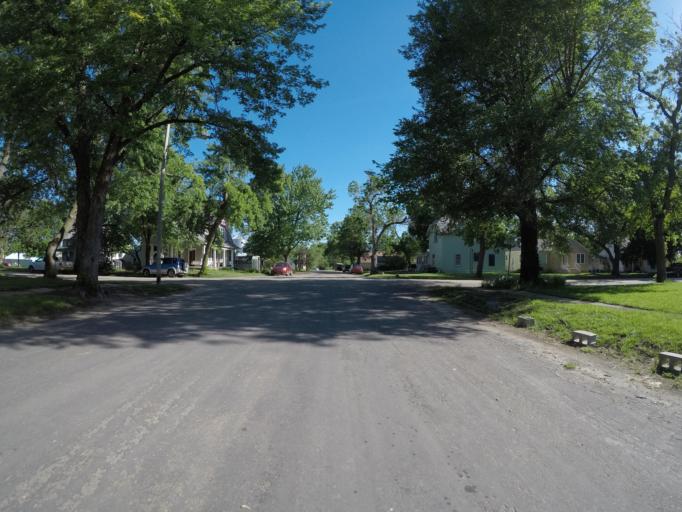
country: US
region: Kansas
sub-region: Riley County
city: Fort Riley North
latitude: 39.3656
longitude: -96.8603
